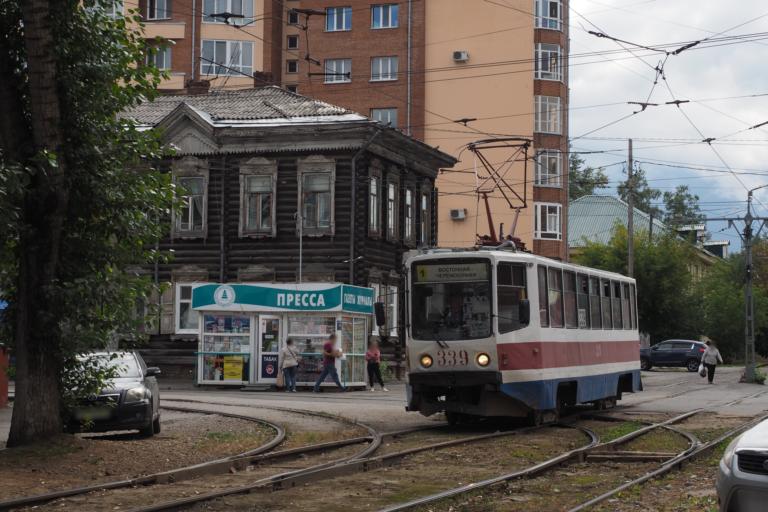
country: RU
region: Tomsk
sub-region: Tomskiy Rayon
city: Tomsk
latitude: 56.4797
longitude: 84.9530
